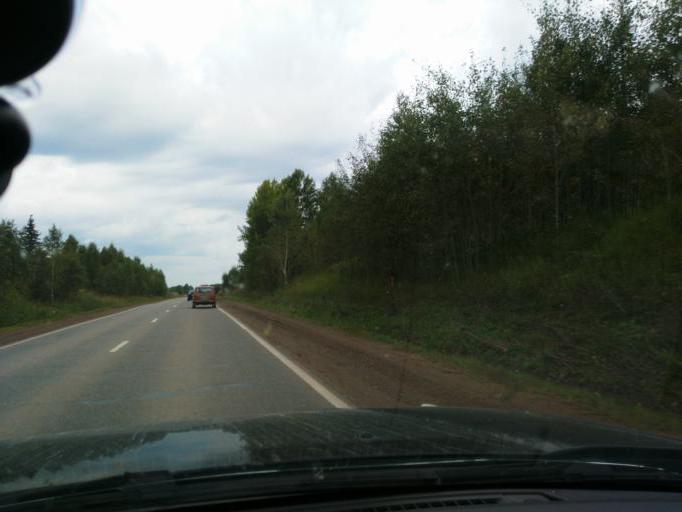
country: RU
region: Perm
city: Chernushka
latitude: 56.7425
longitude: 56.1633
